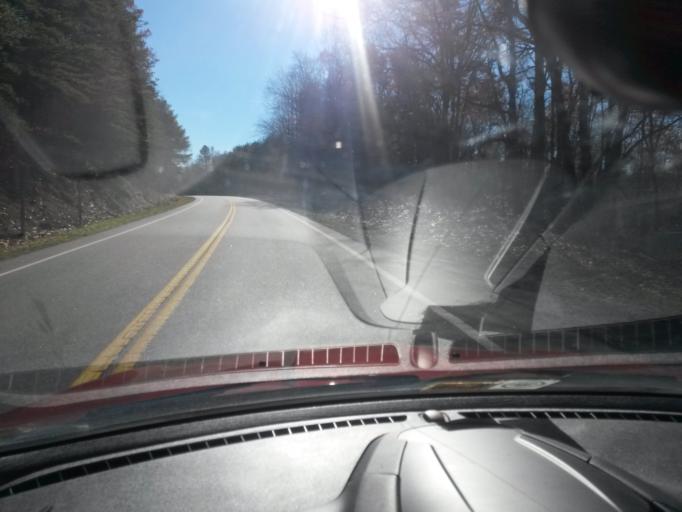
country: US
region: Virginia
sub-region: Henry County
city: Pannill Fork
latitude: 36.7564
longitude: -80.0905
